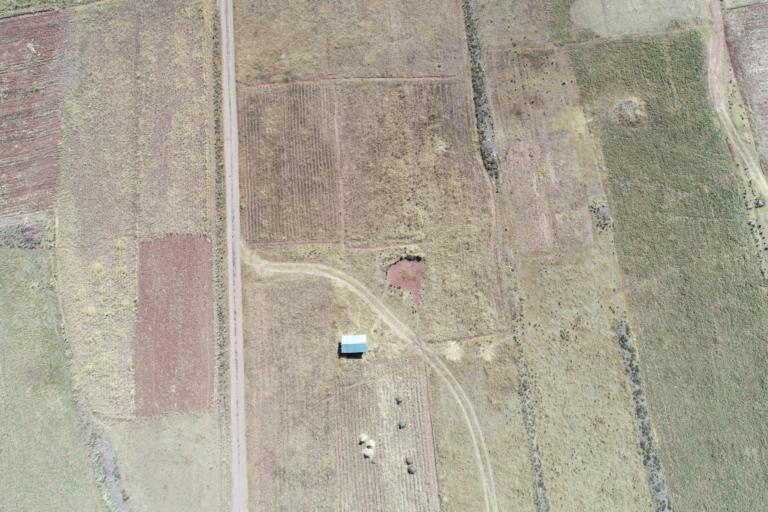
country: BO
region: La Paz
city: Tiahuanaco
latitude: -16.5958
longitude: -68.7816
